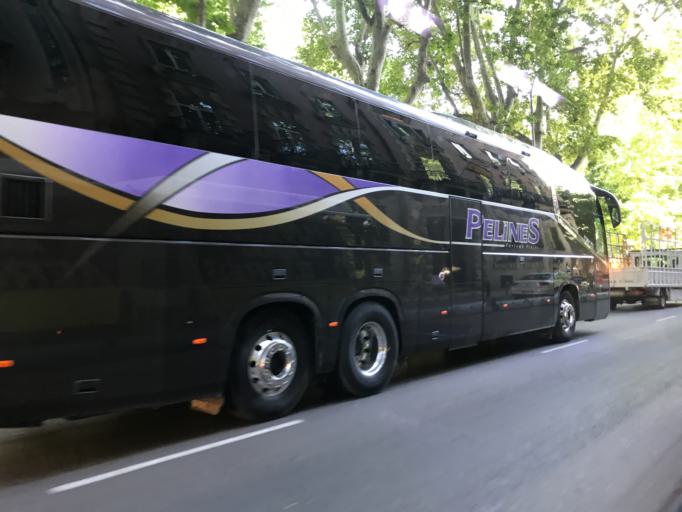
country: ES
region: Madrid
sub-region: Provincia de Madrid
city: Madrid
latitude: 40.4171
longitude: -3.6943
